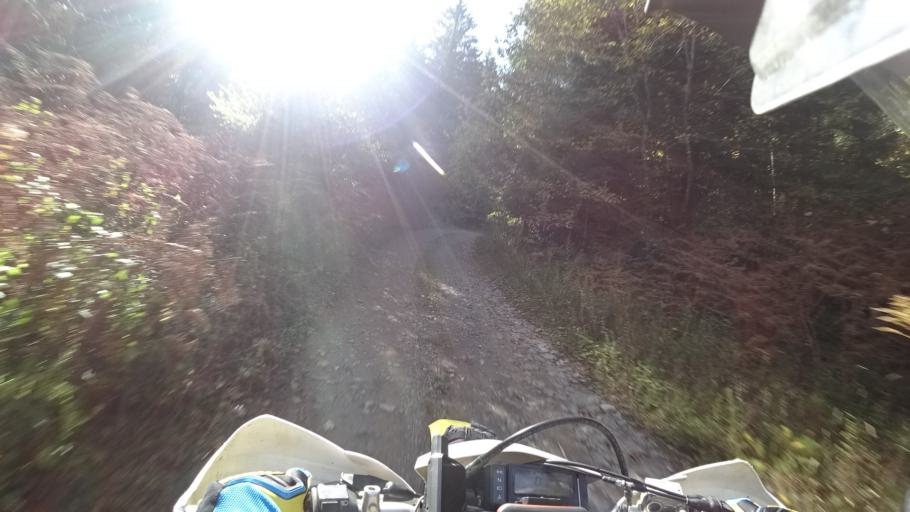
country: HR
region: Karlovacka
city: Plaski
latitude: 45.0664
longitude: 15.3473
